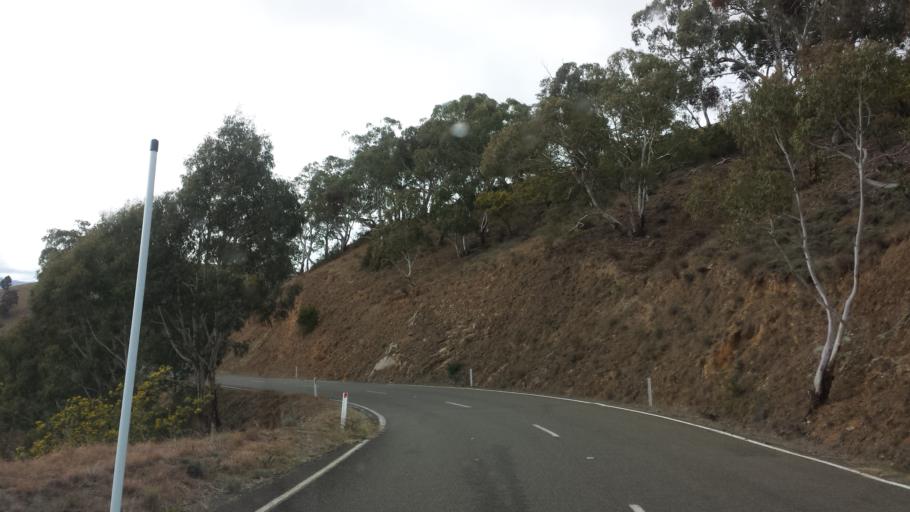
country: AU
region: Victoria
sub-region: Alpine
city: Mount Beauty
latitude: -37.1152
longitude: 147.5587
